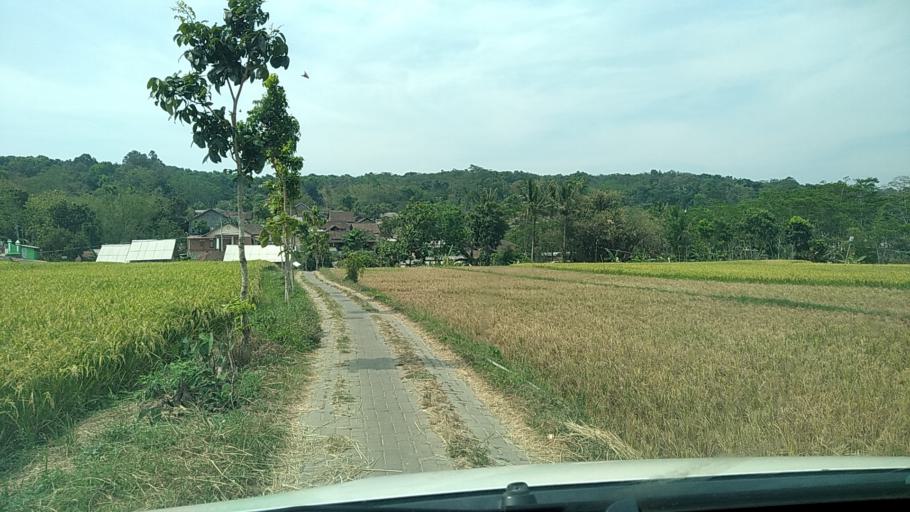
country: ID
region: Central Java
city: Ungaran
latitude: -7.0797
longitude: 110.3175
